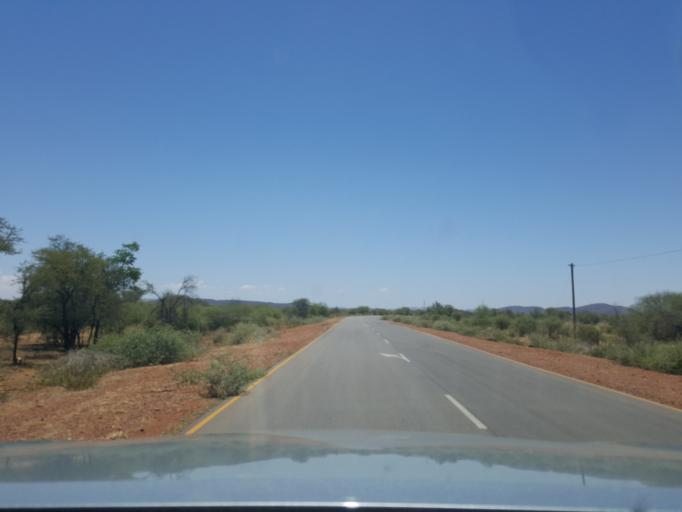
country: BW
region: South East
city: Ramotswa
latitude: -25.0089
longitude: 25.9026
